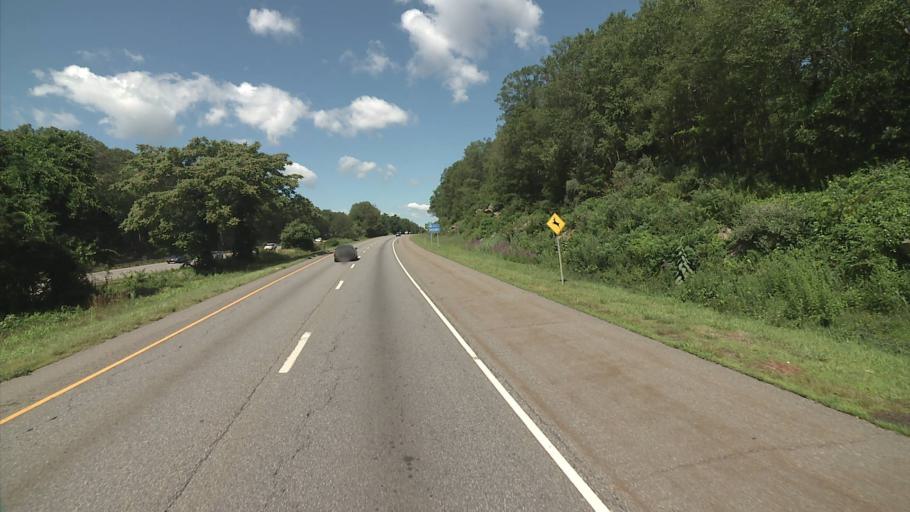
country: US
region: Connecticut
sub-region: New London County
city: Old Mystic
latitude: 41.3723
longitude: -71.9320
